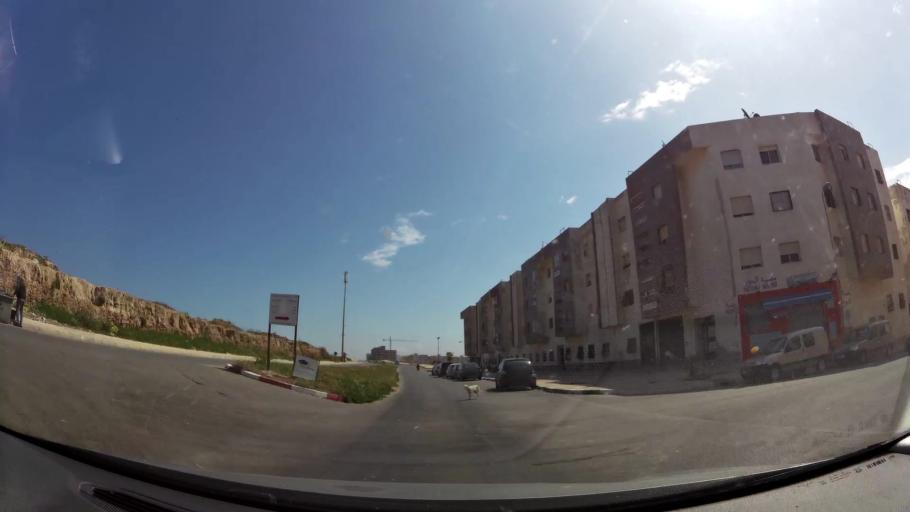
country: MA
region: Rabat-Sale-Zemmour-Zaer
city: Sale
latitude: 34.0827
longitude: -6.7896
